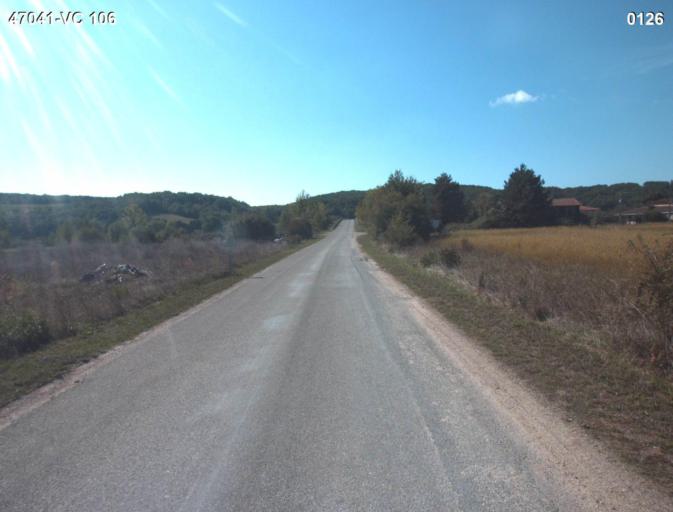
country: FR
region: Aquitaine
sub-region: Departement du Lot-et-Garonne
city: Port-Sainte-Marie
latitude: 44.2172
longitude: 0.3917
